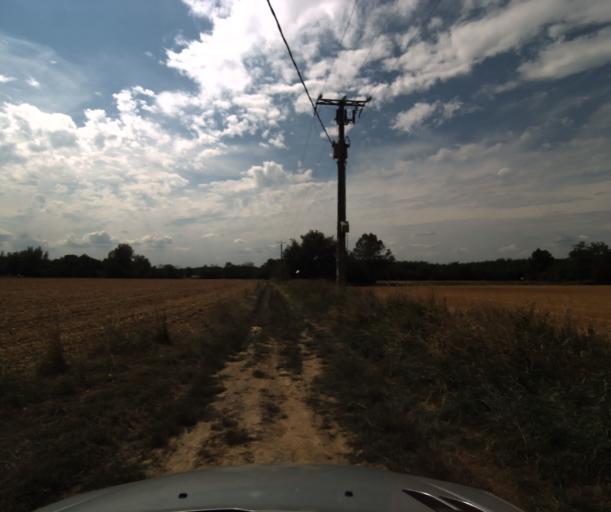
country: FR
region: Midi-Pyrenees
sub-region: Departement de la Haute-Garonne
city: Labastidette
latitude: 43.4869
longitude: 1.2247
